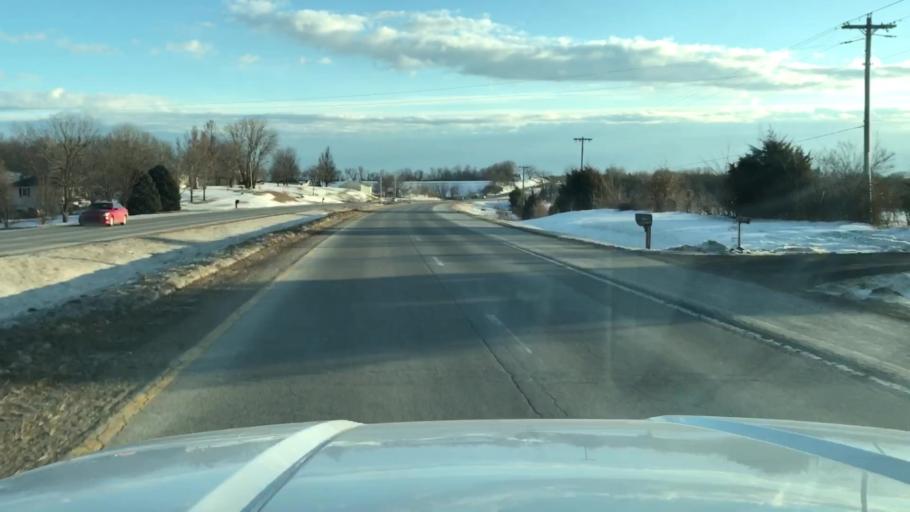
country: US
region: Missouri
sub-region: Andrew County
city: Country Club Village
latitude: 39.8687
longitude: -94.8084
